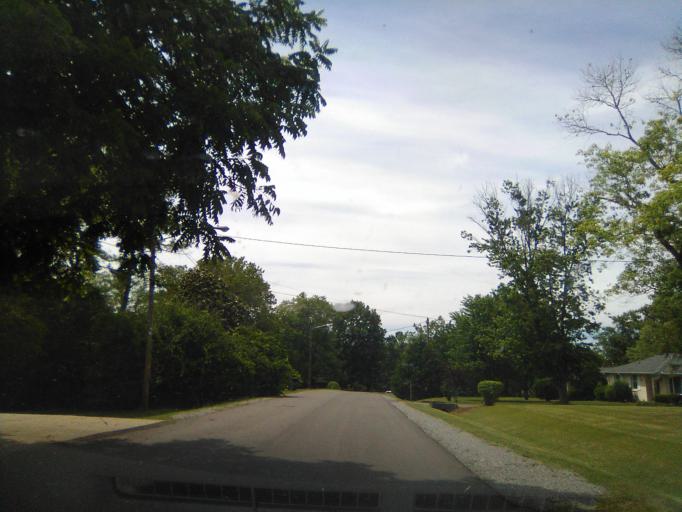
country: US
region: Tennessee
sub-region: Davidson County
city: Belle Meade
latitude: 36.1247
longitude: -86.9004
